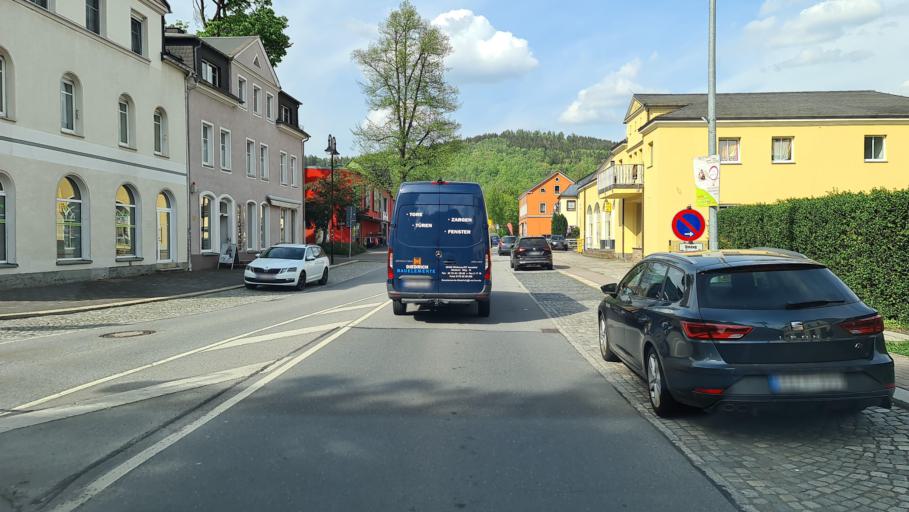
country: DE
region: Saxony
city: Schwarzenberg
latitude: 50.5424
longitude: 12.7879
